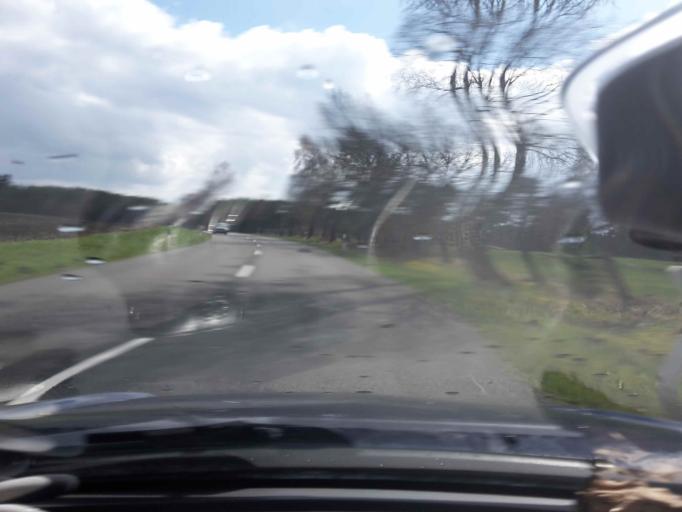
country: DE
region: Lower Saxony
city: Bispingen
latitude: 53.0746
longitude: 9.9670
